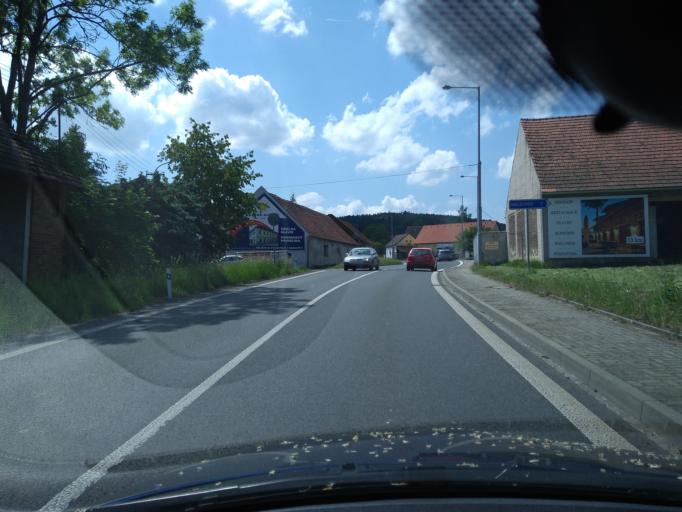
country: CZ
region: Plzensky
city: Svihov
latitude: 49.4484
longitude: 13.2881
